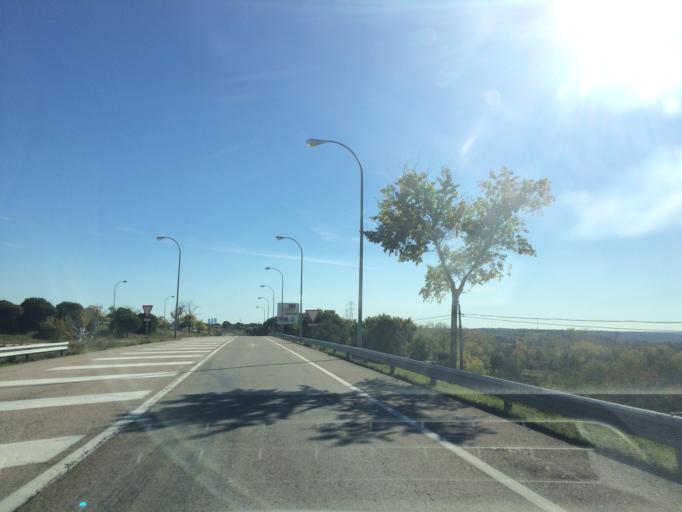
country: ES
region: Madrid
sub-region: Provincia de Madrid
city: Tres Cantos
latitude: 40.6078
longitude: -3.7223
